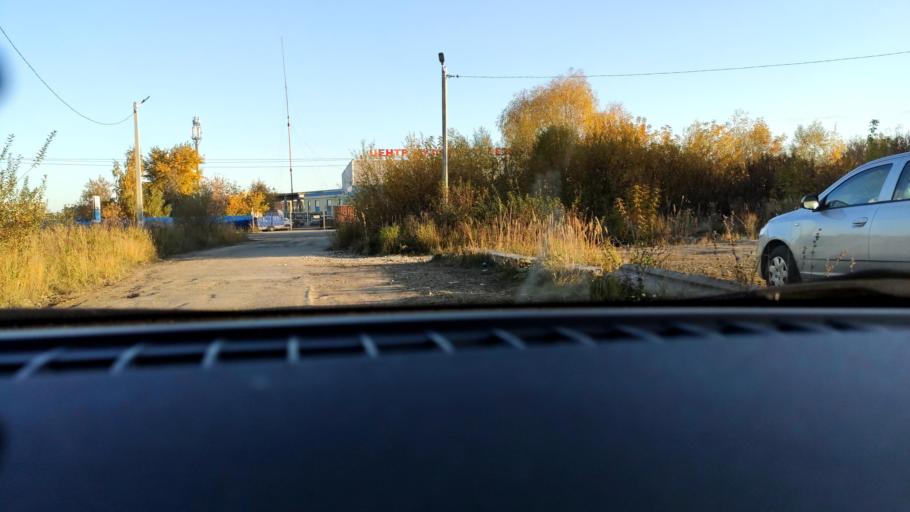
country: RU
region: Perm
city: Froly
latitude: 57.9556
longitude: 56.2739
